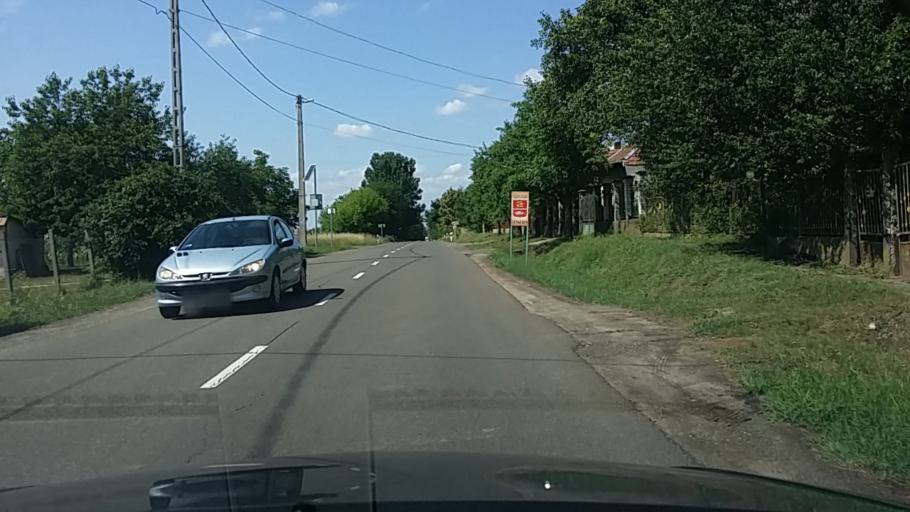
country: HU
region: Komarom-Esztergom
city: Esztergom
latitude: 47.8888
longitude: 18.7759
